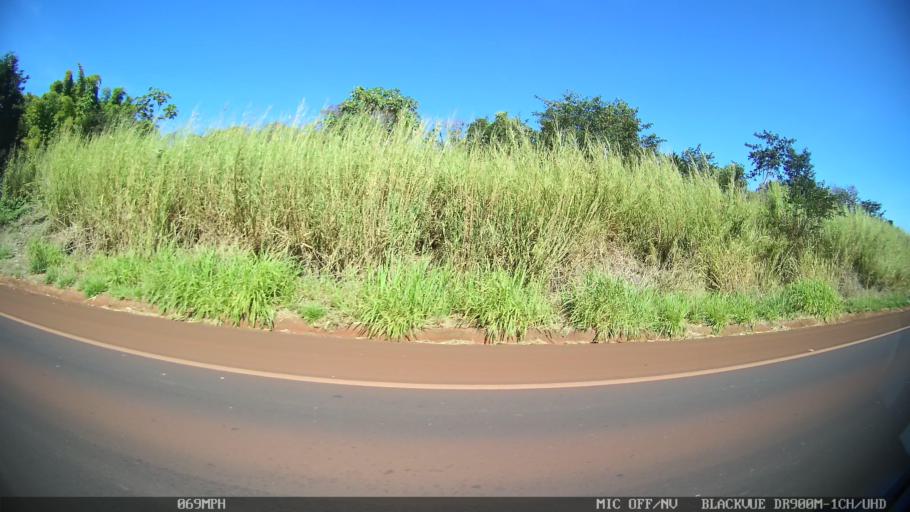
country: BR
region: Sao Paulo
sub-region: Ipua
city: Ipua
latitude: -20.4931
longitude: -48.0202
